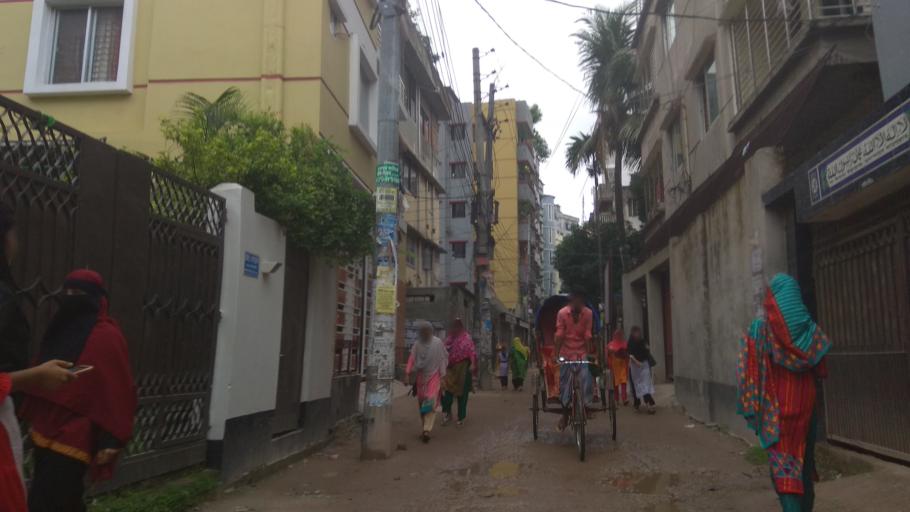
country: BD
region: Dhaka
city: Azimpur
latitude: 23.8025
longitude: 90.3745
